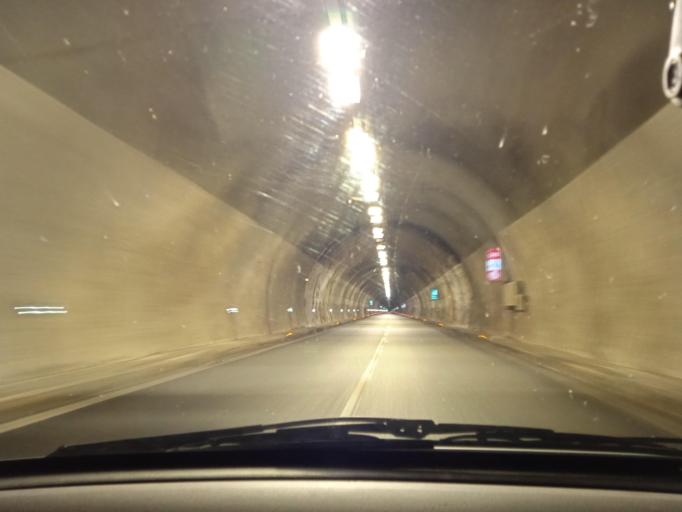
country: IT
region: Sicily
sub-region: Messina
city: Capo d'Orlando
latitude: 38.1469
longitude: 14.7599
